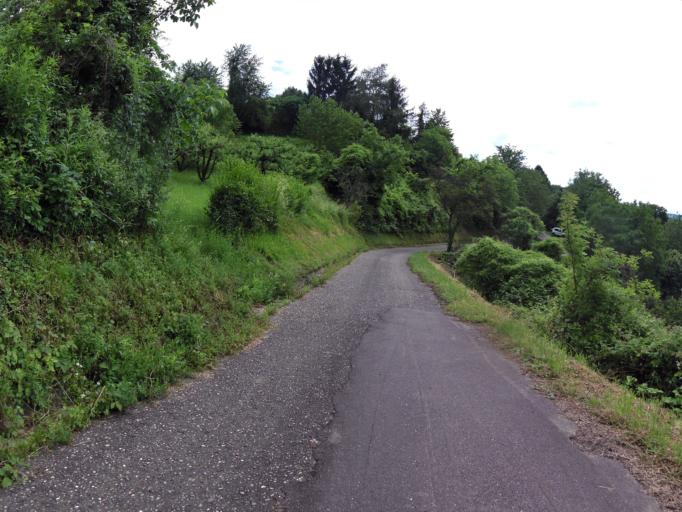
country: DE
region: Baden-Wuerttemberg
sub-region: Freiburg Region
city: Lahr
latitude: 48.3542
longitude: 7.8518
